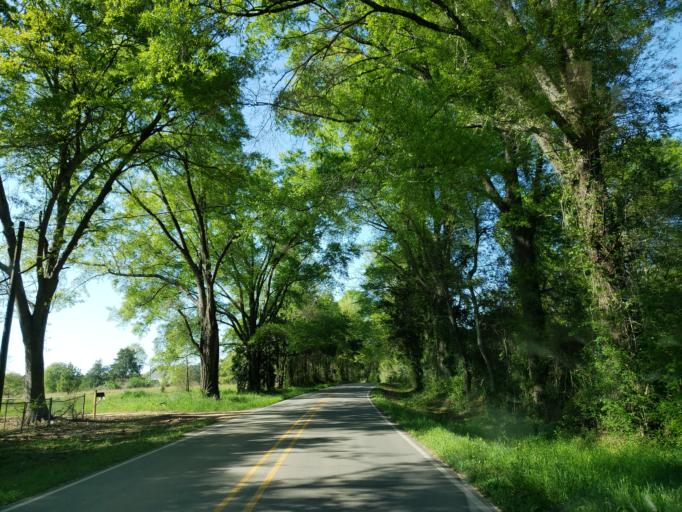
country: US
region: Mississippi
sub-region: Forrest County
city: Rawls Springs
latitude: 31.5416
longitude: -89.3652
